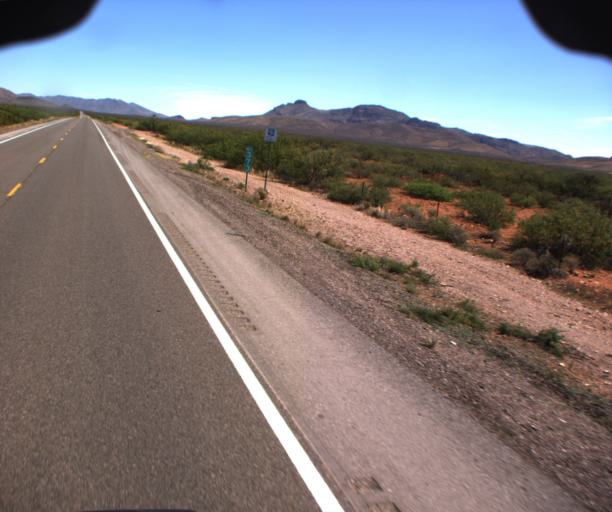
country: US
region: Arizona
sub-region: Cochise County
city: Douglas
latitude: 31.4142
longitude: -109.4950
